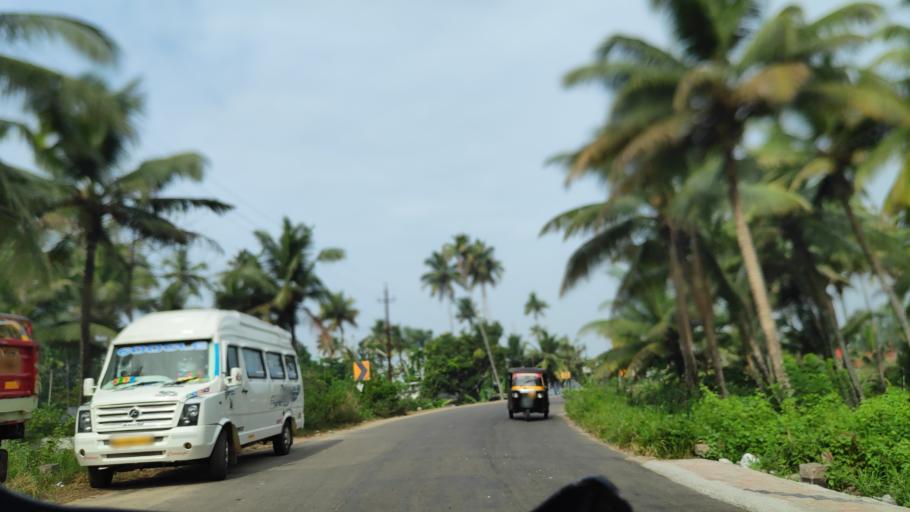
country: IN
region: Kerala
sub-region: Alappuzha
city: Kutiatodu
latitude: 9.7946
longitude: 76.3547
